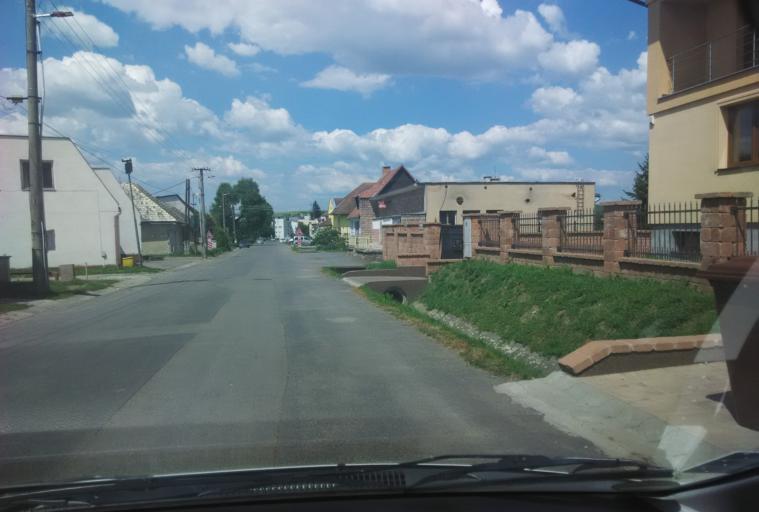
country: SK
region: Banskobystricky
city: Dudince
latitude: 48.1670
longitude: 18.8942
